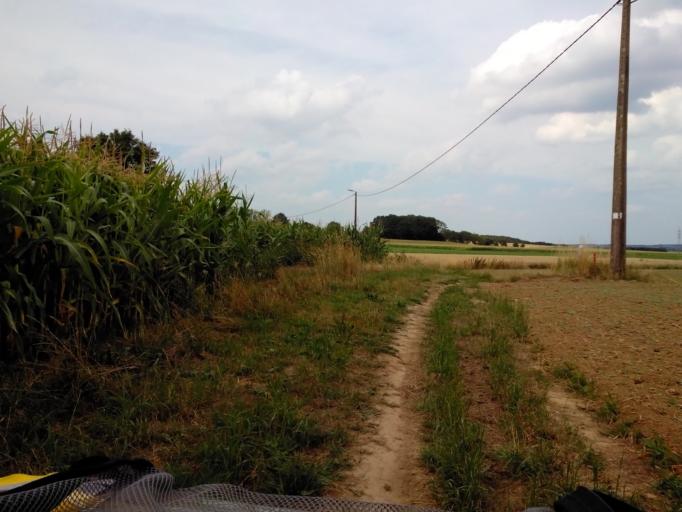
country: BE
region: Flanders
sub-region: Provincie Vlaams-Brabant
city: Holsbeek
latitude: 50.9031
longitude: 4.7887
